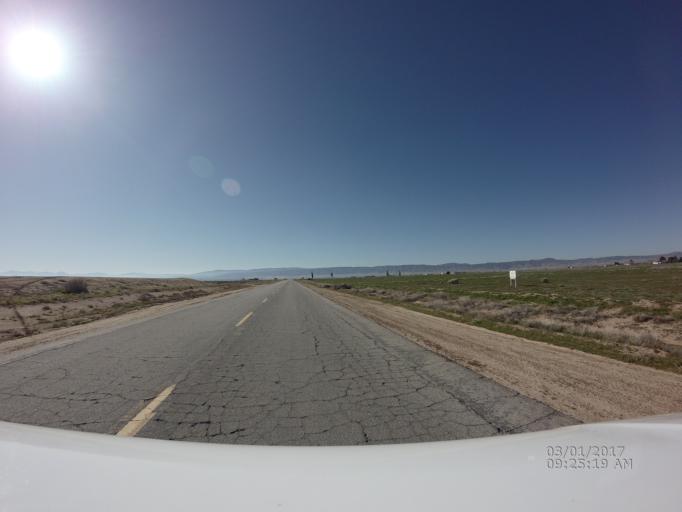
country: US
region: California
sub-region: Los Angeles County
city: Quartz Hill
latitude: 34.7408
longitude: -118.2726
